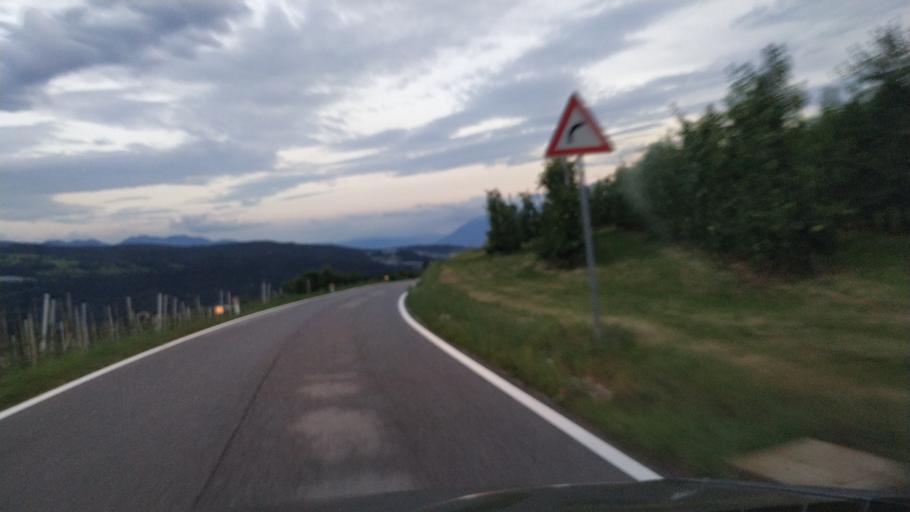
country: IT
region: Trentino-Alto Adige
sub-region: Provincia di Trento
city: Brez
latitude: 46.4390
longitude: 11.1115
